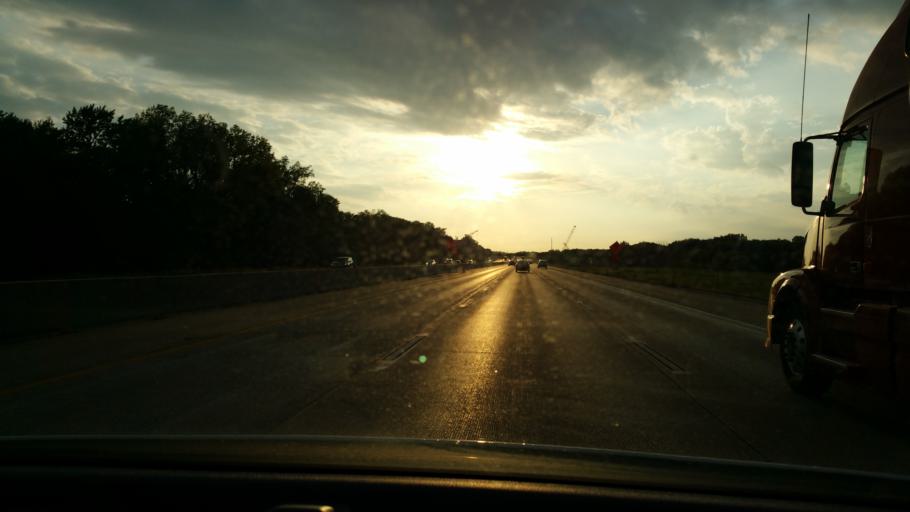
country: US
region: Iowa
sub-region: Polk County
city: Johnston
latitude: 41.6512
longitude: -93.6733
